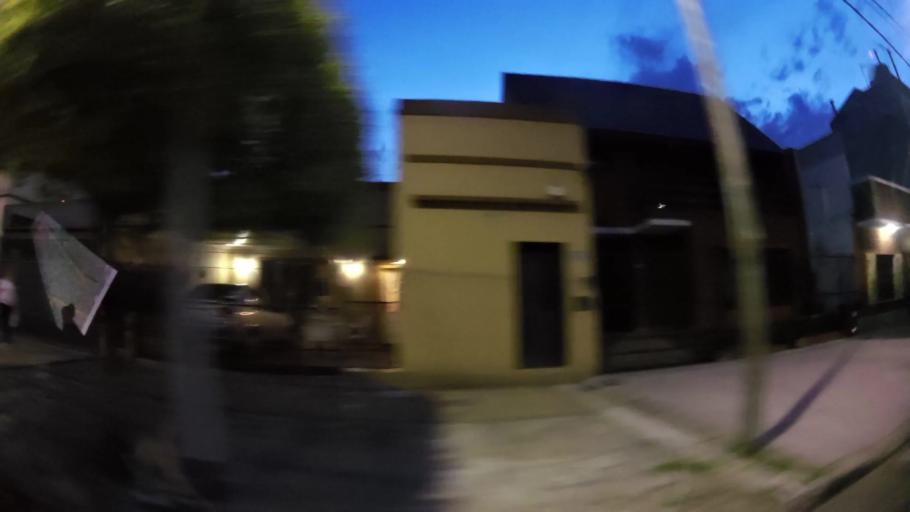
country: AR
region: Buenos Aires
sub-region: Partido de Avellaneda
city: Avellaneda
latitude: -34.6955
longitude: -58.3222
